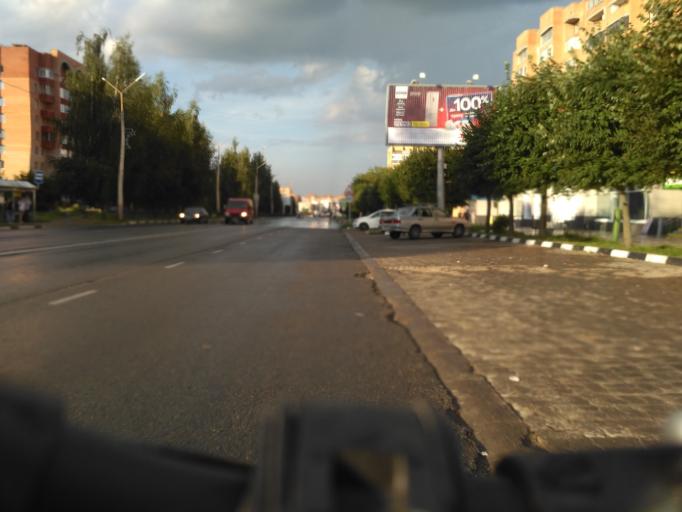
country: RU
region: Moskovskaya
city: Dubna
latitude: 56.7320
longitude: 37.1499
